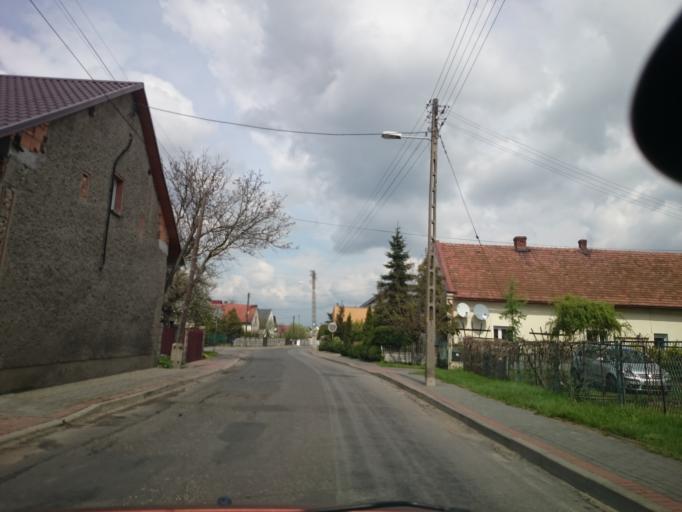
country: PL
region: Opole Voivodeship
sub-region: Powiat opolski
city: Naklo
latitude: 50.5136
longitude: 18.1215
